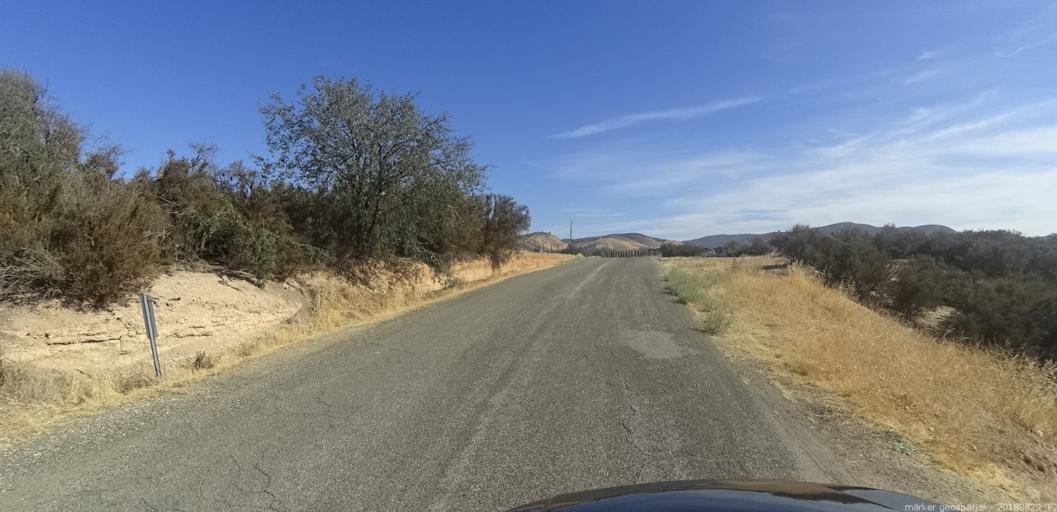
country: US
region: California
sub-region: Monterey County
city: King City
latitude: 35.9762
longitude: -121.1176
